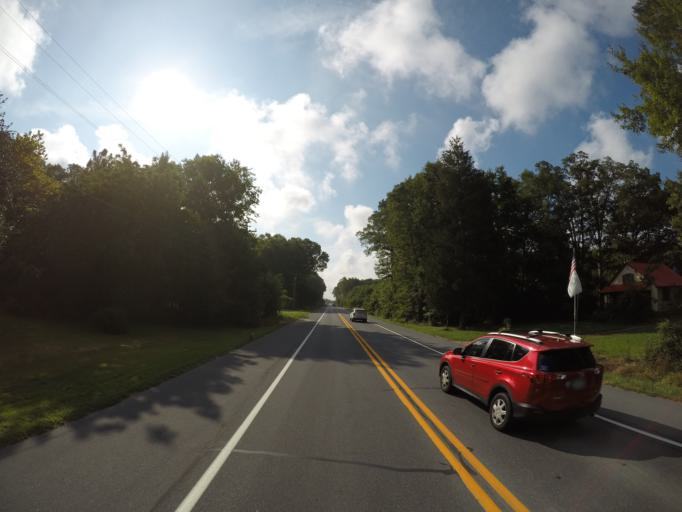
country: US
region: Delaware
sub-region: Sussex County
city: Bridgeville
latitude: 38.7638
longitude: -75.6430
